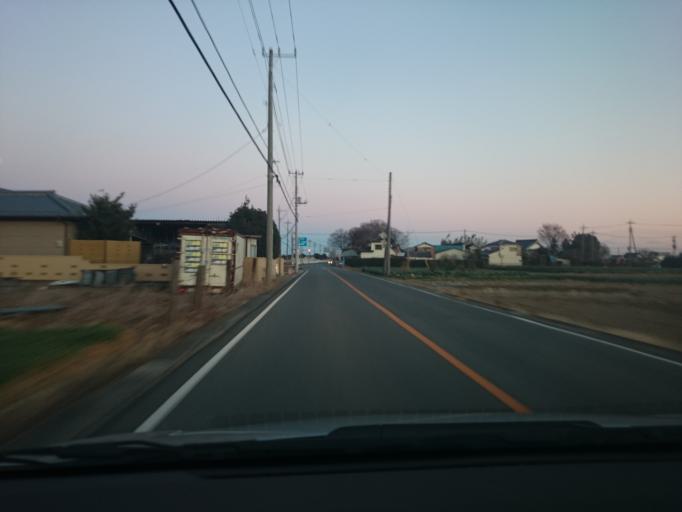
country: JP
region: Saitama
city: Fukayacho
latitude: 36.2293
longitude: 139.3134
